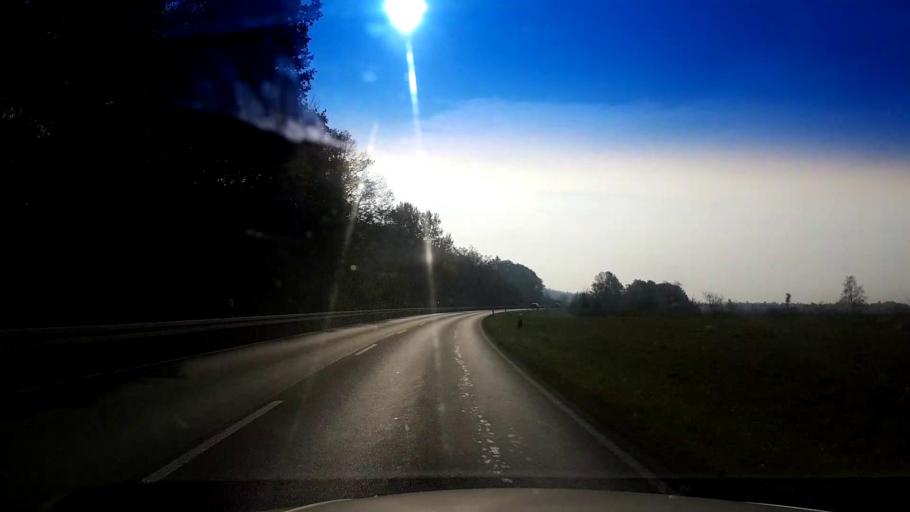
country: DE
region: Bavaria
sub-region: Upper Franconia
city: Neuenmarkt
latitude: 50.0984
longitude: 11.6057
